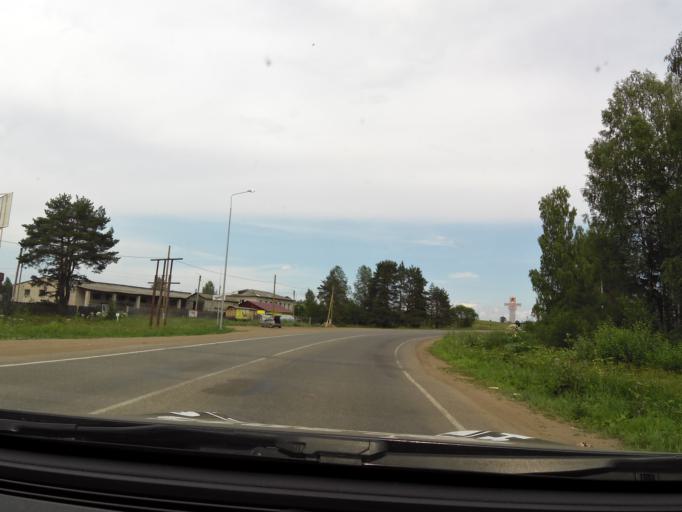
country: RU
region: Kirov
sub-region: Kirovo-Chepetskiy Rayon
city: Kirov
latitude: 58.6230
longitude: 49.7811
